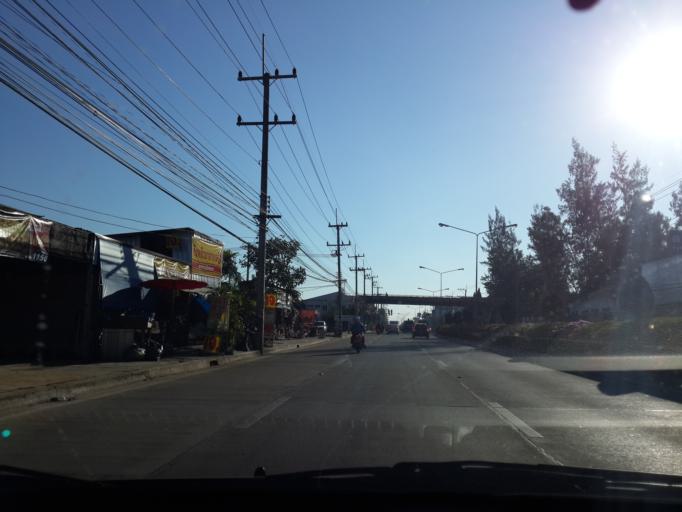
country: TH
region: Chiang Mai
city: Hang Dong
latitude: 18.7153
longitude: 98.9405
